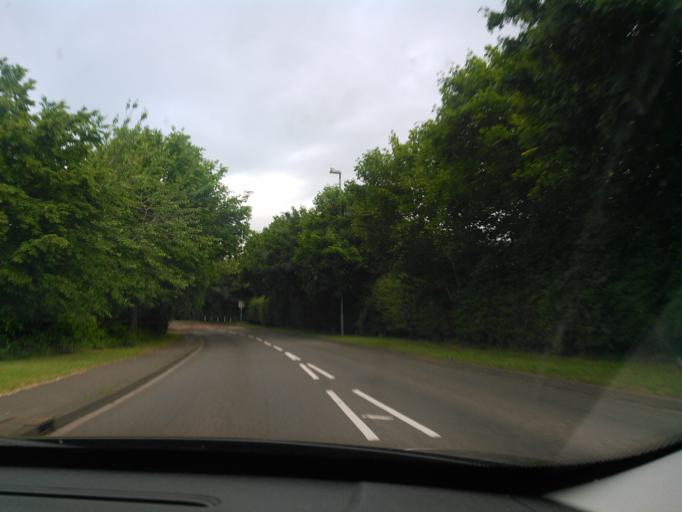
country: GB
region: England
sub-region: Shropshire
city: Shrewsbury
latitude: 52.7423
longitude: -2.7365
